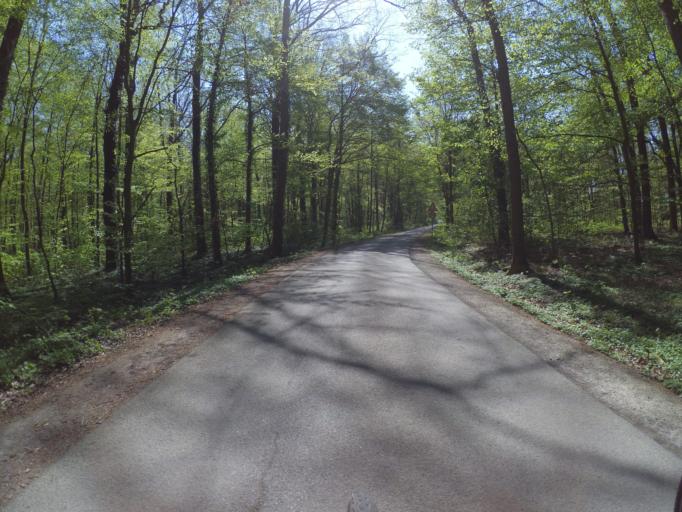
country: DE
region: North Rhine-Westphalia
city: Ludinghausen
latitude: 51.7580
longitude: 7.4407
